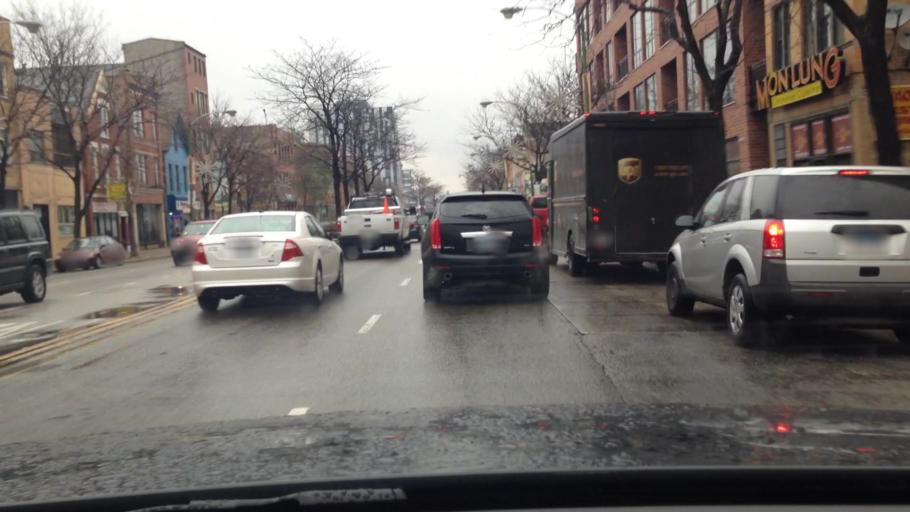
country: US
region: Illinois
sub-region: Cook County
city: Chicago
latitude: 41.8998
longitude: -87.6673
